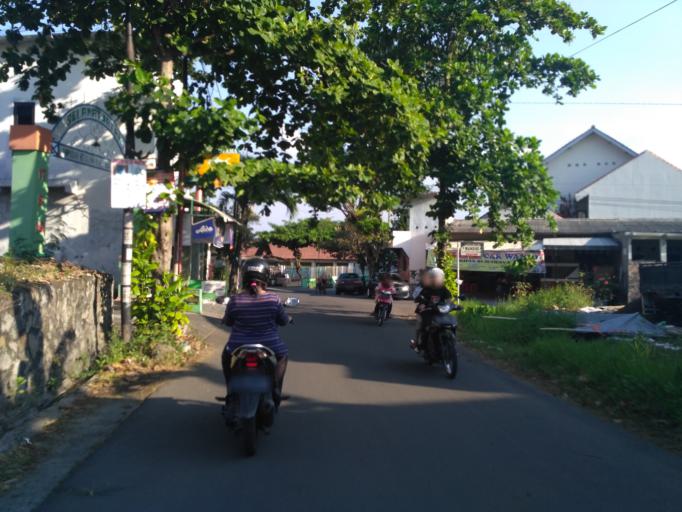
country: ID
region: Central Java
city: Mranggen
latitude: -7.0176
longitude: 110.4662
